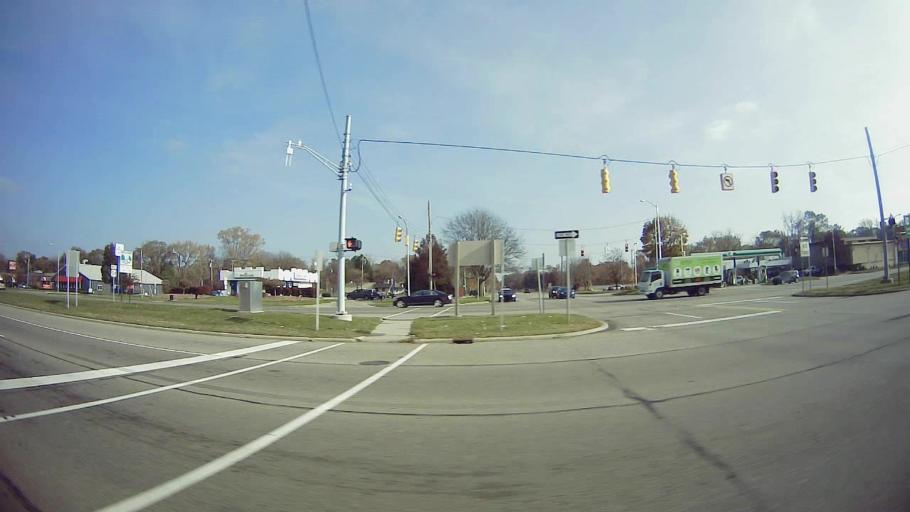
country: US
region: Michigan
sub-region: Oakland County
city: Bingham Farms
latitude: 42.4575
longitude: -83.2787
